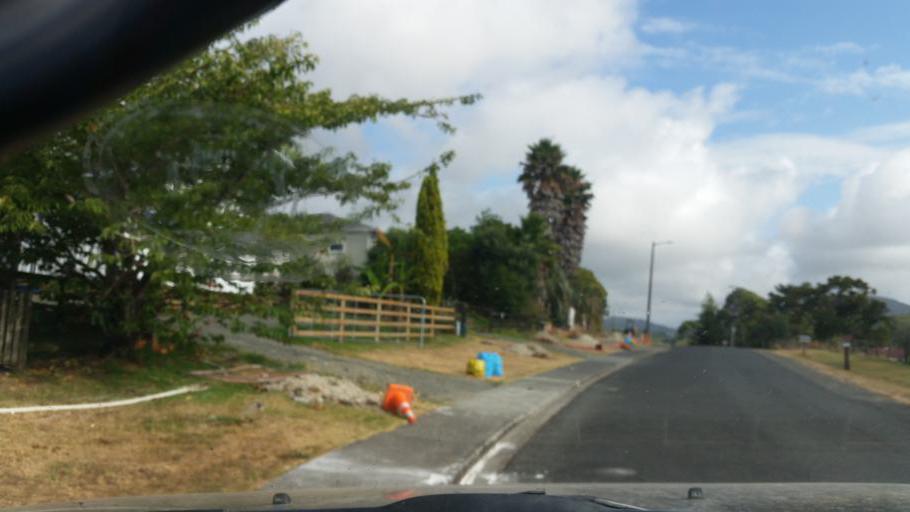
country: NZ
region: Auckland
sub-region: Auckland
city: Wellsford
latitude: -36.1686
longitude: 174.4476
